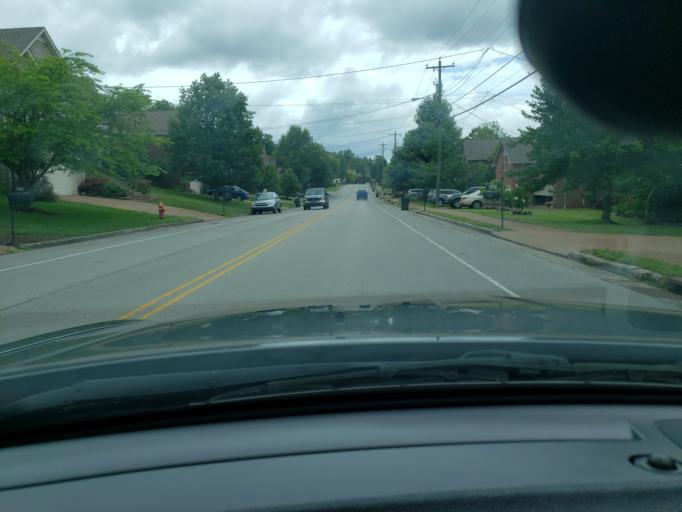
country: US
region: Tennessee
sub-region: Williamson County
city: Nolensville
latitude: 36.0135
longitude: -86.6985
